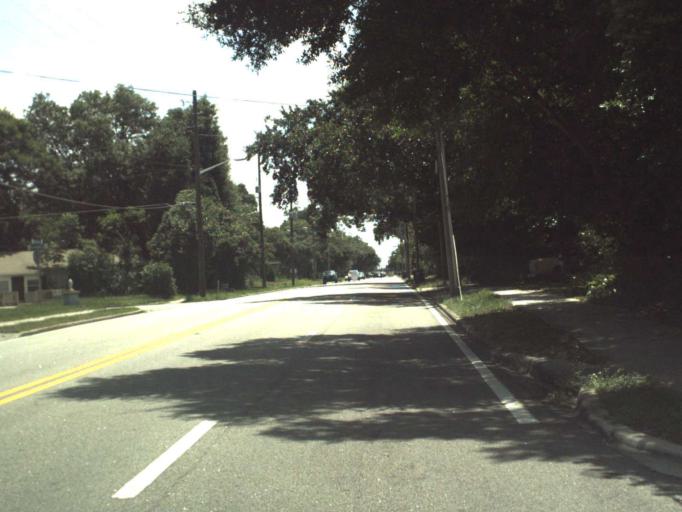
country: US
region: Florida
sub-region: Orange County
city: Orlando
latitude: 28.5458
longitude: -81.3587
